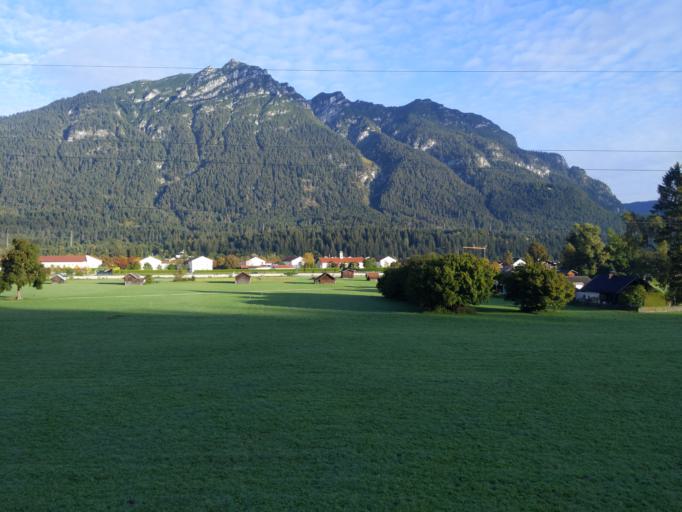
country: DE
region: Bavaria
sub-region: Upper Bavaria
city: Garmisch-Partenkirchen
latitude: 47.4801
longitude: 11.0696
